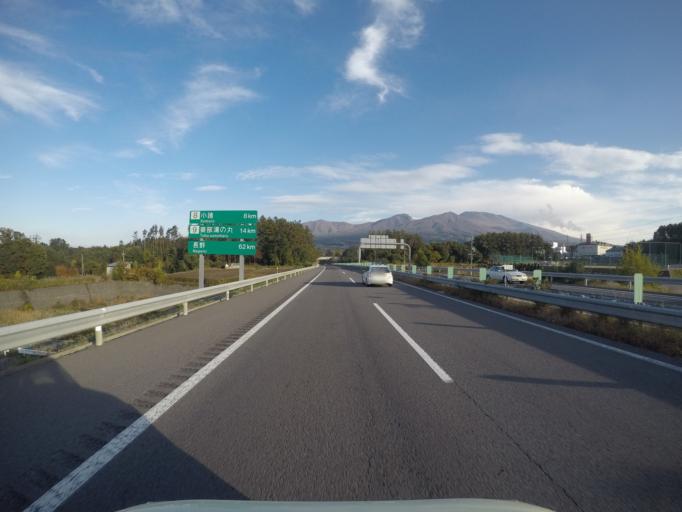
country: JP
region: Nagano
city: Komoro
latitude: 36.3105
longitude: 138.4807
